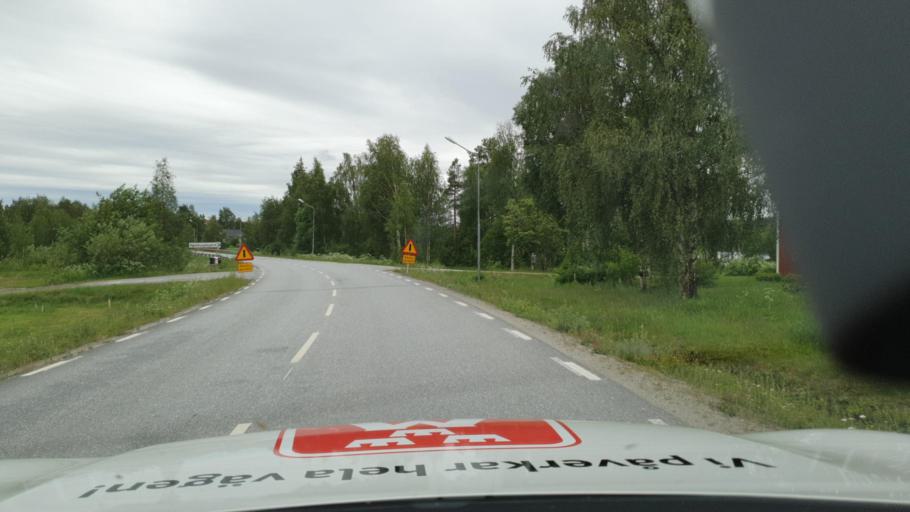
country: SE
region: Vaesterbotten
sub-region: Lycksele Kommun
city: Lycksele
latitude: 64.0817
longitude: 18.3997
